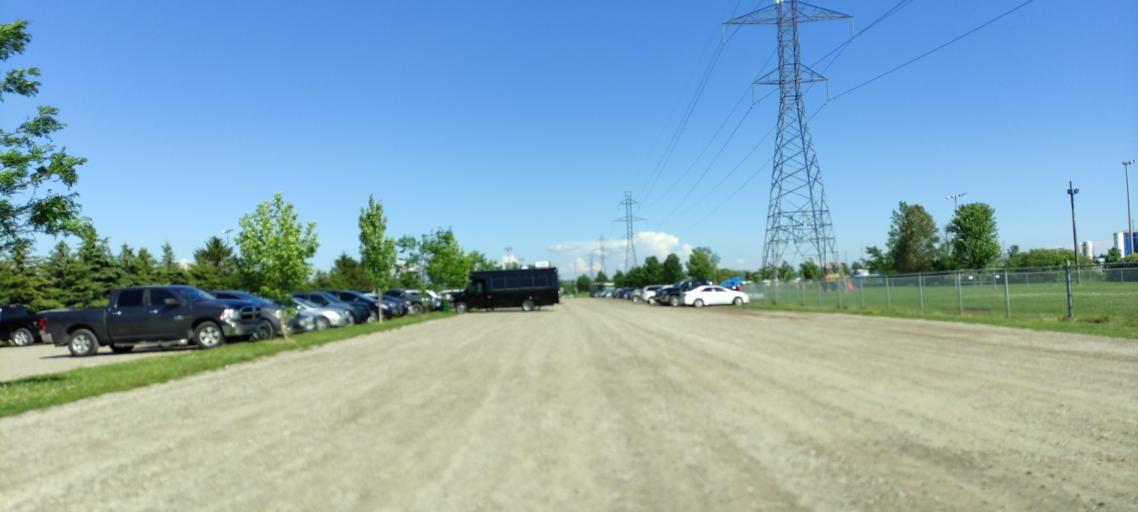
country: CA
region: Ontario
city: Stratford
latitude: 43.3487
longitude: -81.0113
